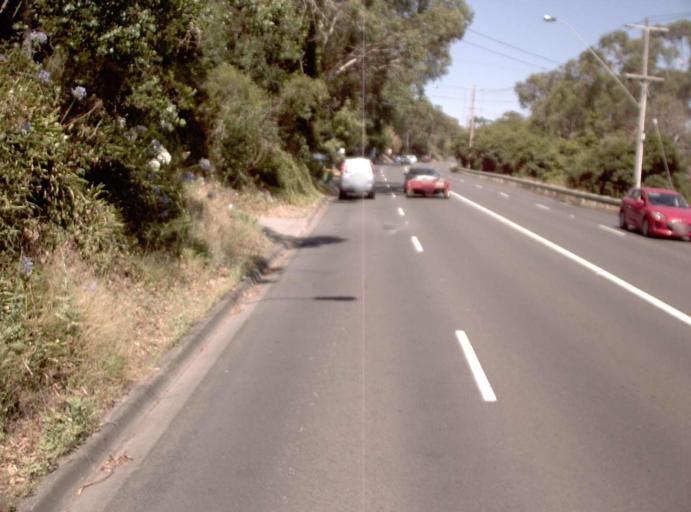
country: AU
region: Victoria
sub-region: Yarra Ranges
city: Tremont
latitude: -37.8956
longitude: 145.3174
